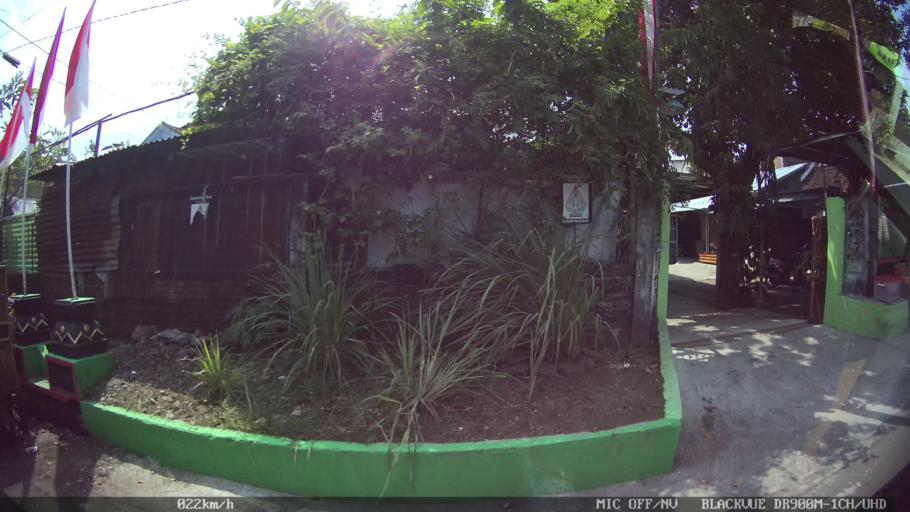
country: ID
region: Daerah Istimewa Yogyakarta
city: Yogyakarta
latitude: -7.8048
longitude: 110.3869
